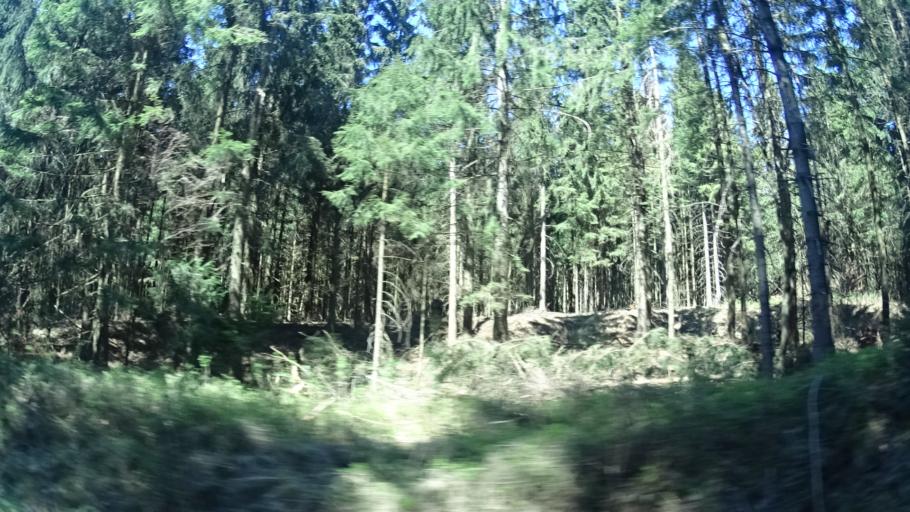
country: DE
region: Thuringia
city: Frauenwald
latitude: 50.5316
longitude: 10.8577
